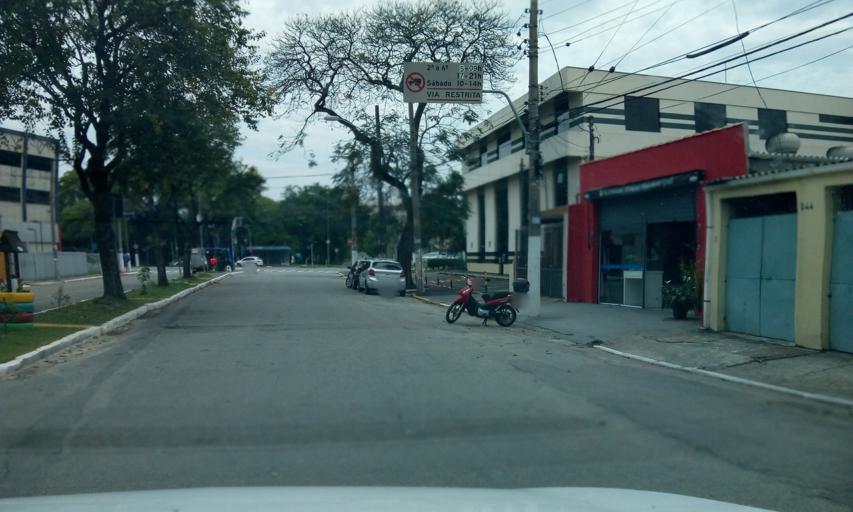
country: BR
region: Sao Paulo
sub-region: Sao Paulo
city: Sao Paulo
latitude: -23.5154
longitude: -46.7002
